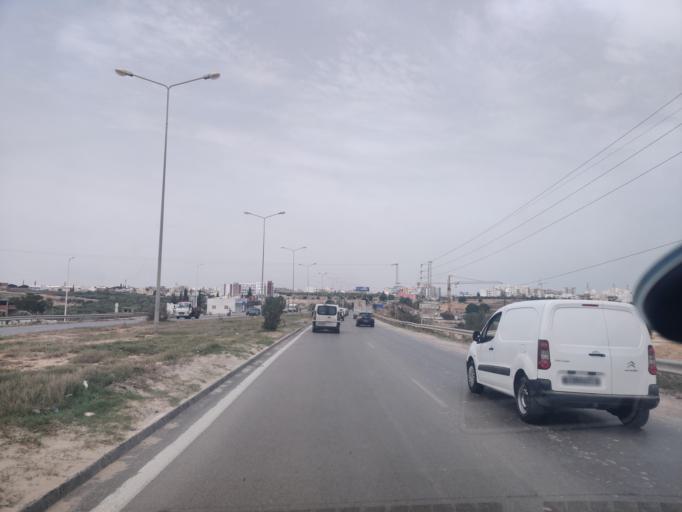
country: TN
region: Susah
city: Hammam Sousse
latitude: 35.8223
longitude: 10.5938
